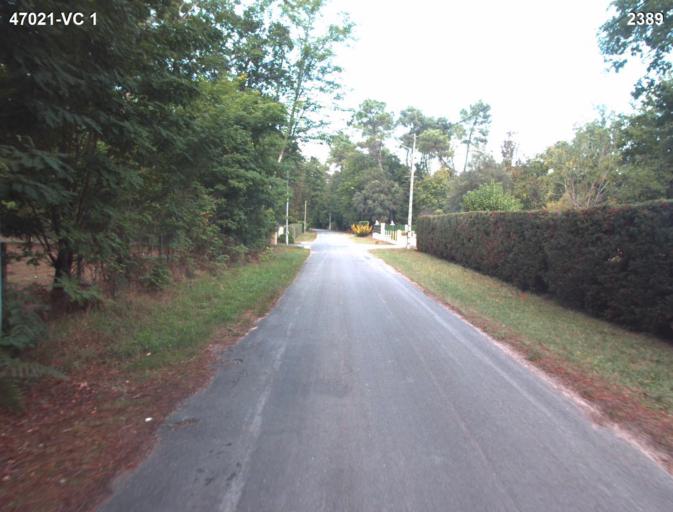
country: FR
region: Aquitaine
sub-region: Departement du Lot-et-Garonne
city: Barbaste
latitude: 44.1464
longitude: 0.2953
